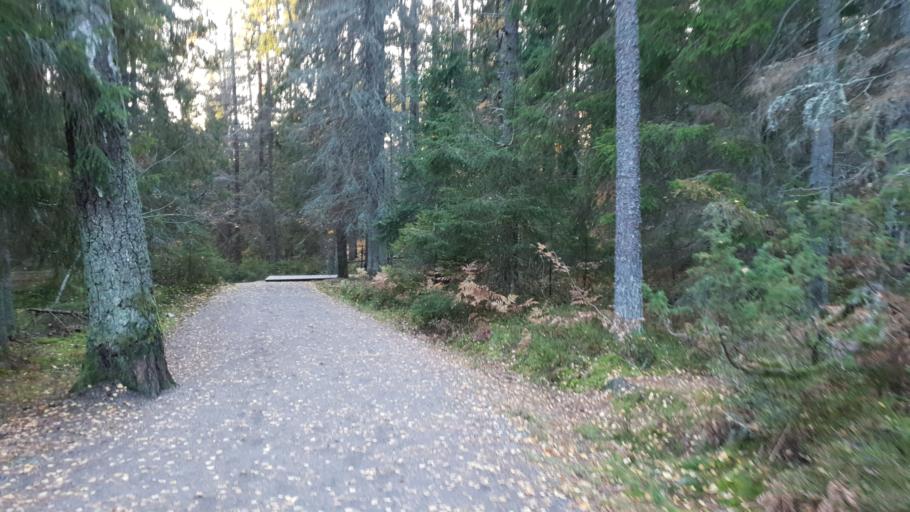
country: SE
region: Stockholm
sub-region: Tyreso Kommun
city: Bollmora
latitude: 59.1722
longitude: 18.2397
